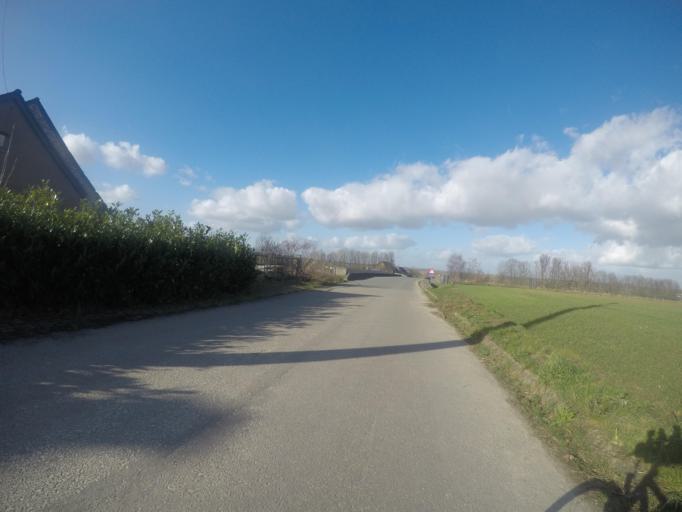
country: BE
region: Wallonia
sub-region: Province du Brabant Wallon
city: Rebecq-Rognon
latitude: 50.6837
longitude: 4.1478
